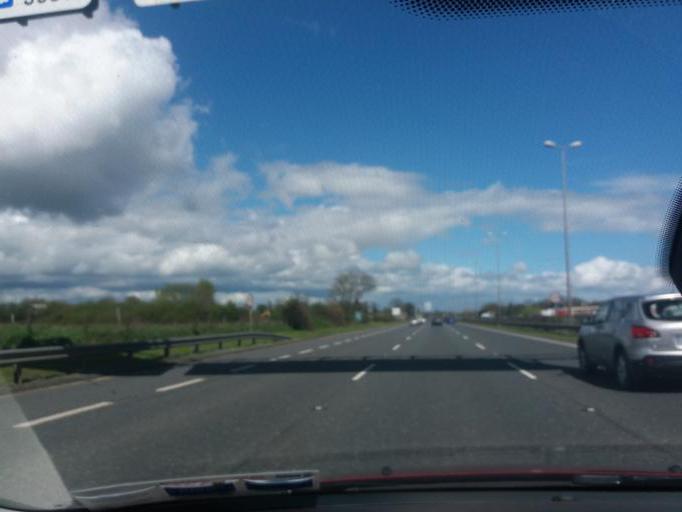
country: IE
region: Leinster
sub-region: South Dublin
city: Saggart
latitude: 53.2962
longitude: -6.4266
